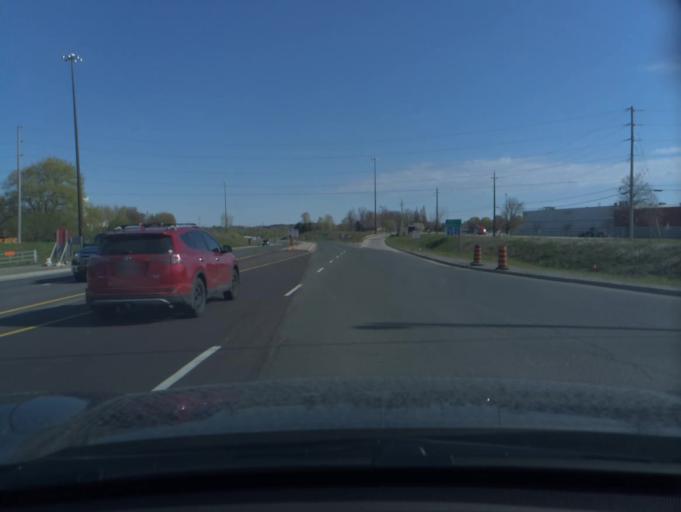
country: CA
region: Ontario
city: North Perth
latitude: 43.8313
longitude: -81.0001
